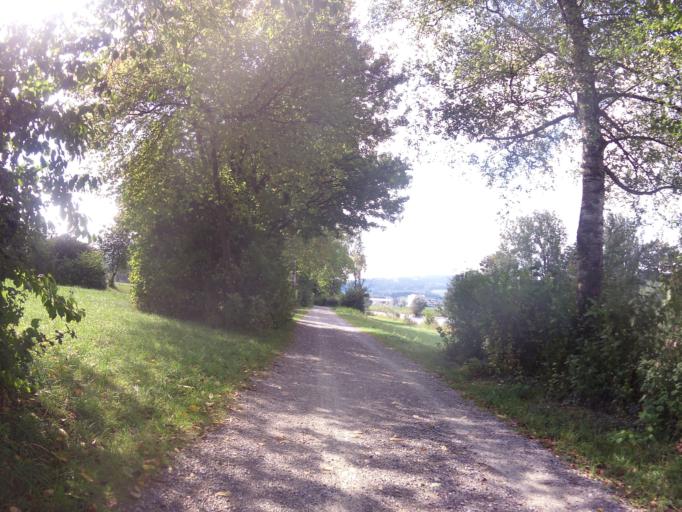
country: CH
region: Zurich
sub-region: Bezirk Dietikon
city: Schlieren / Engstingerquartier
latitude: 47.4051
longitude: 8.4384
